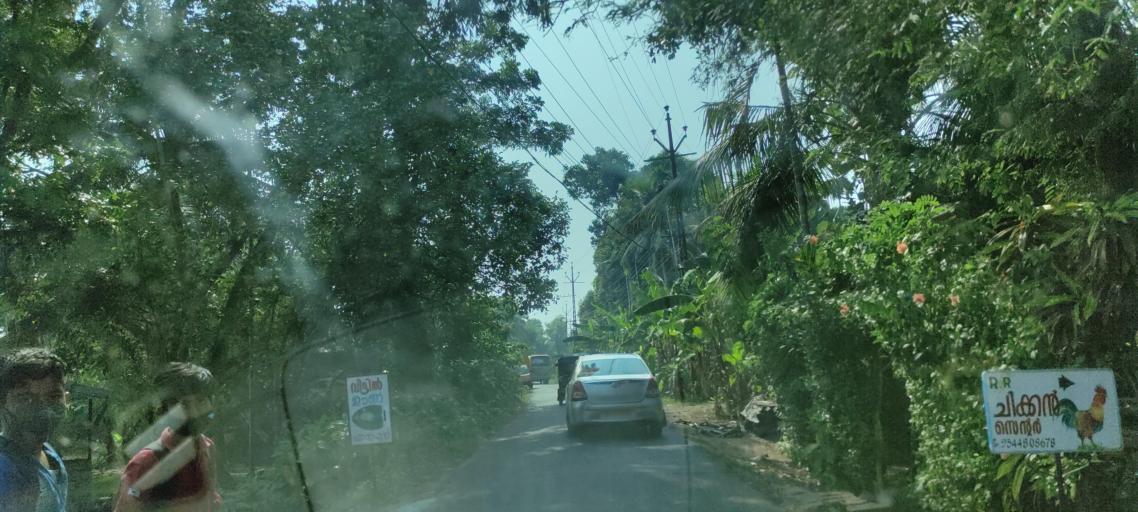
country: IN
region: Kerala
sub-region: Pattanamtitta
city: Tiruvalla
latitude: 9.3556
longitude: 76.5221
